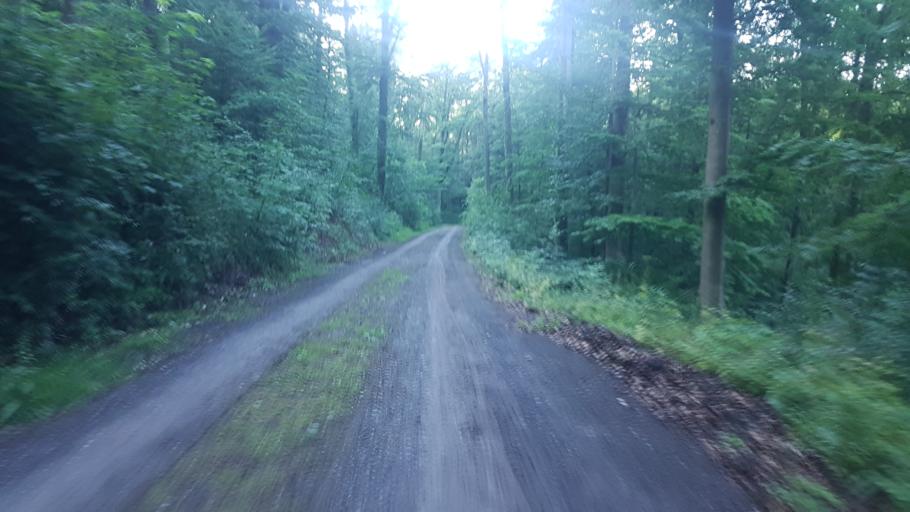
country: DE
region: Baden-Wuerttemberg
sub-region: Karlsruhe Region
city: Sternenfels
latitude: 49.0481
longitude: 8.8789
